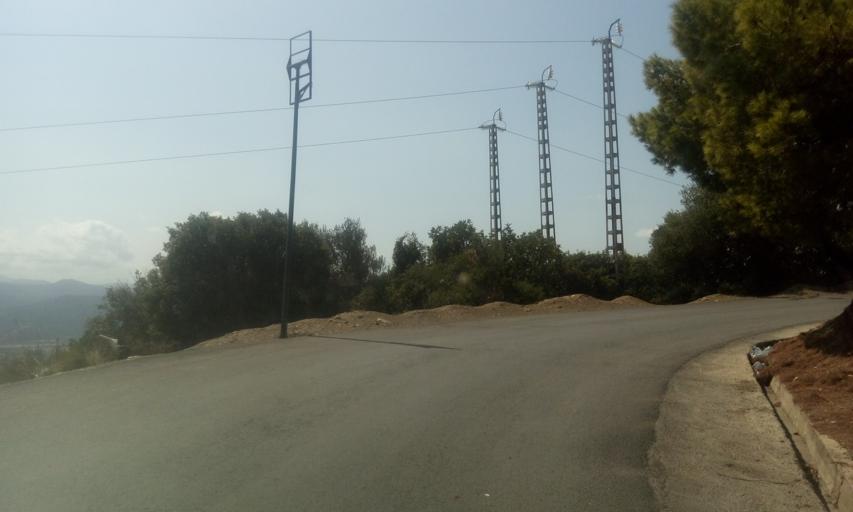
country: DZ
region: Bejaia
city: Bejaia
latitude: 36.7622
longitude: 5.0836
